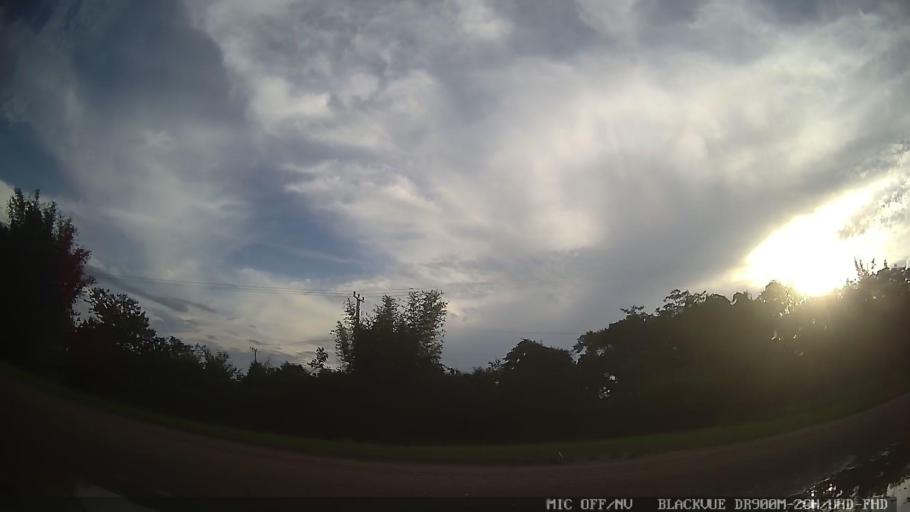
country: BR
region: Sao Paulo
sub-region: Boituva
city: Boituva
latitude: -23.1930
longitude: -47.6285
